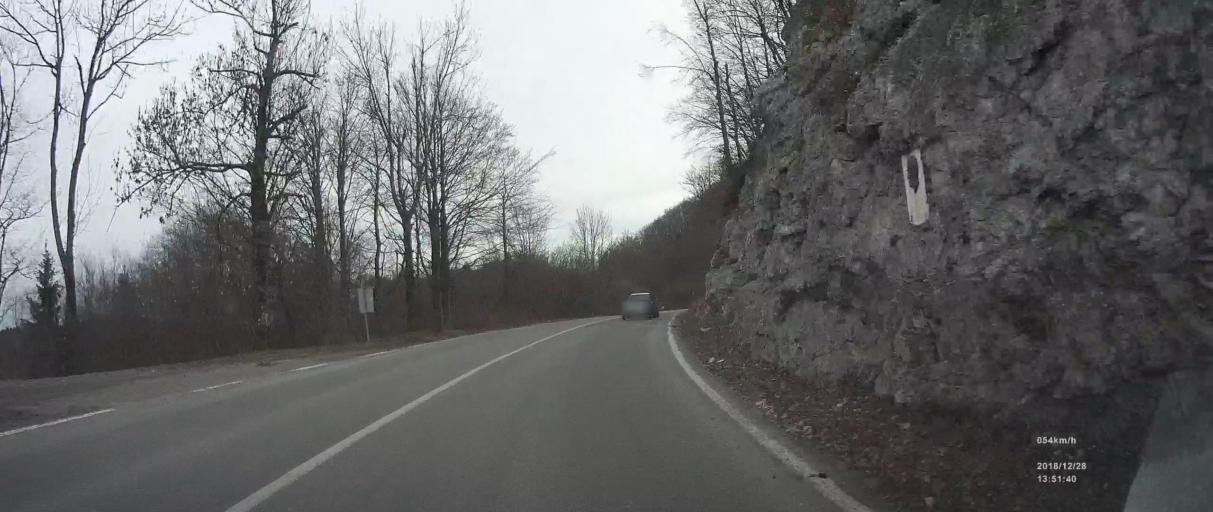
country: HR
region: Primorsko-Goranska
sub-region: Grad Delnice
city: Delnice
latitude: 45.3951
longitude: 14.8416
